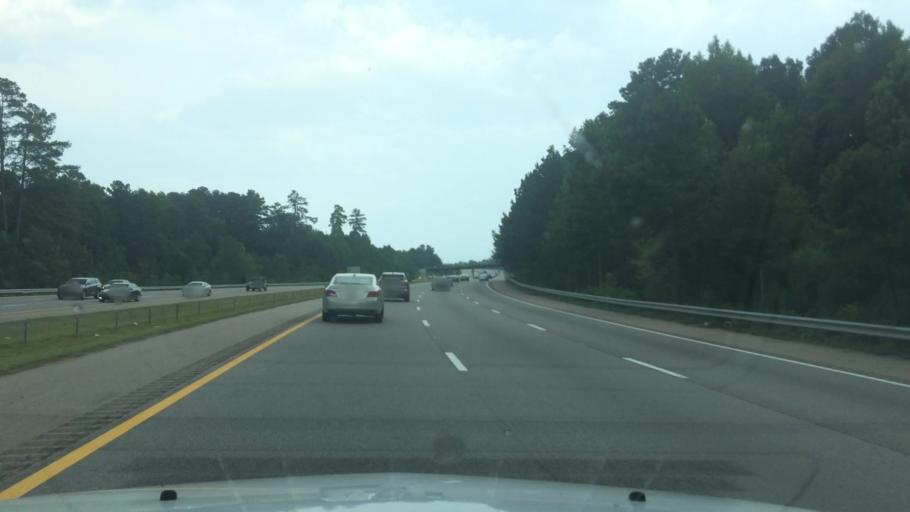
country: US
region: North Carolina
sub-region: Wake County
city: Wake Forest
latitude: 35.8893
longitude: -78.5934
